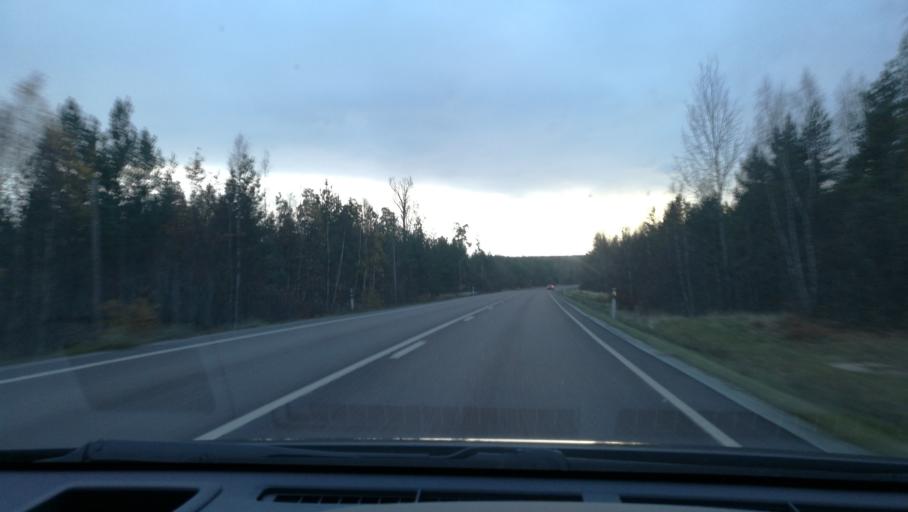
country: SE
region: Vaestmanland
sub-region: Kungsors Kommun
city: Kungsoer
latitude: 59.2584
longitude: 16.1167
